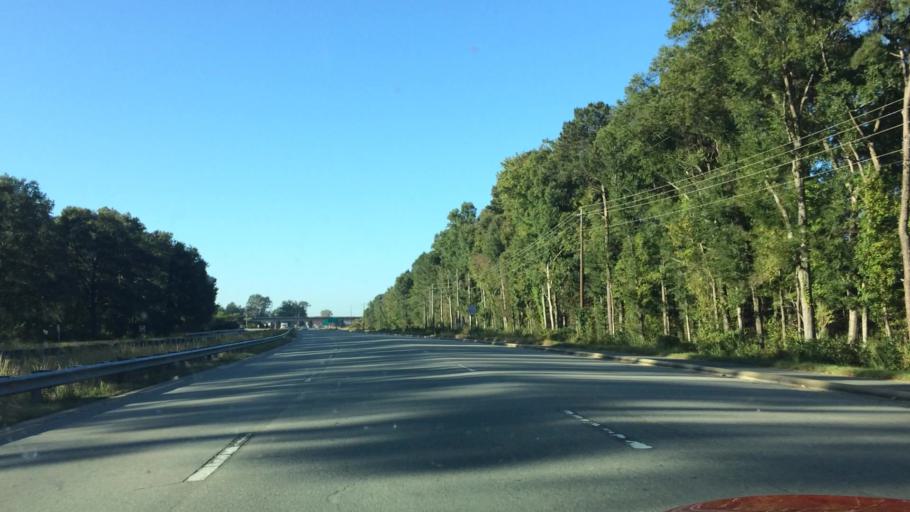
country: US
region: North Carolina
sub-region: Wayne County
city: Goldsboro
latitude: 35.3935
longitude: -78.0061
